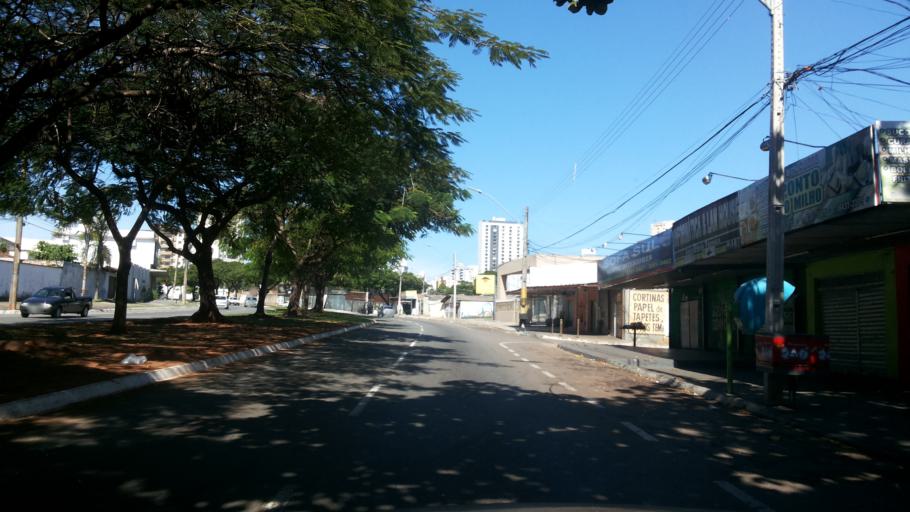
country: BR
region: Goias
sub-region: Goiania
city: Goiania
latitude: -16.7070
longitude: -49.2506
